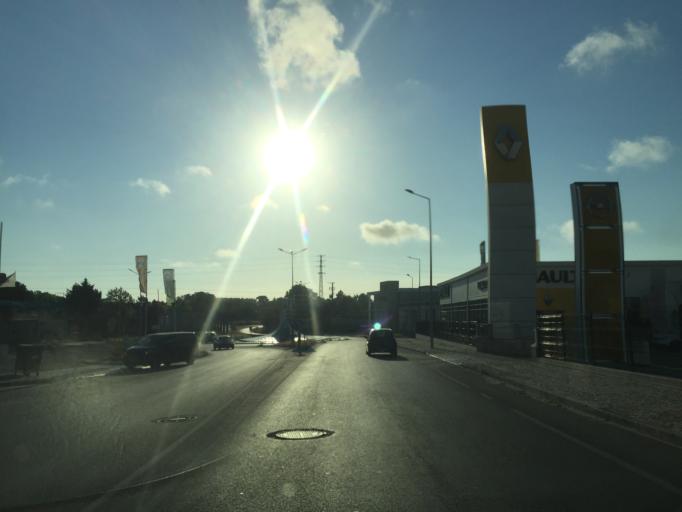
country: PT
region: Leiria
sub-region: Caldas da Rainha
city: Caldas da Rainha
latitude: 39.4063
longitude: -9.1520
